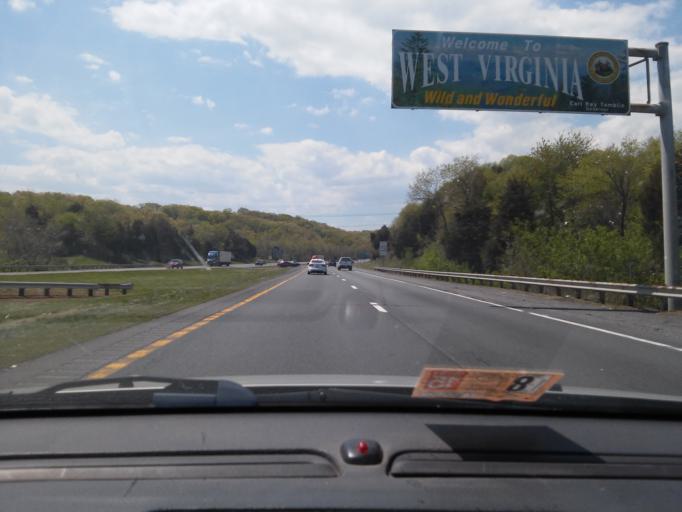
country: US
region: Maryland
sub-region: Washington County
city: Williamsport
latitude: 39.5847
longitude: -77.8317
